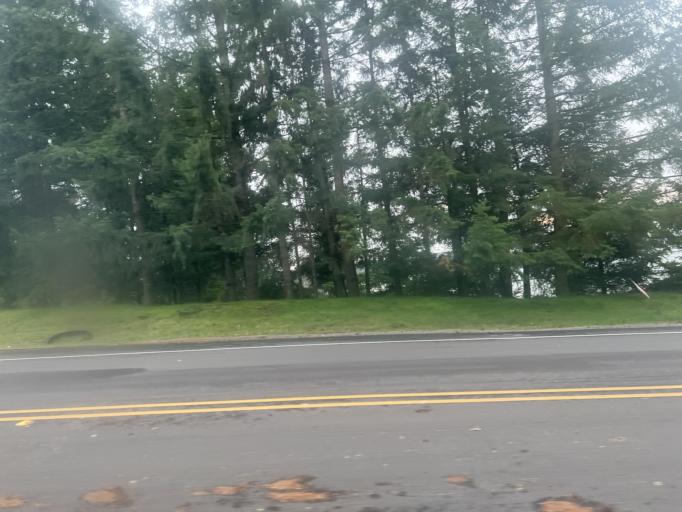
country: US
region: Oregon
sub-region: Clackamas County
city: Wilsonville
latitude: 45.3356
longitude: -122.7572
